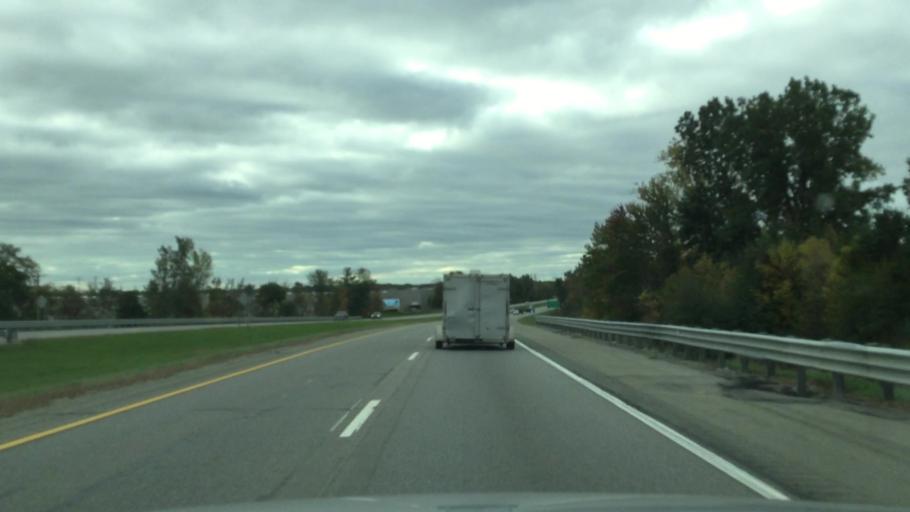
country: US
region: Michigan
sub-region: Macomb County
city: Shelby
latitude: 42.6832
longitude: -83.0161
